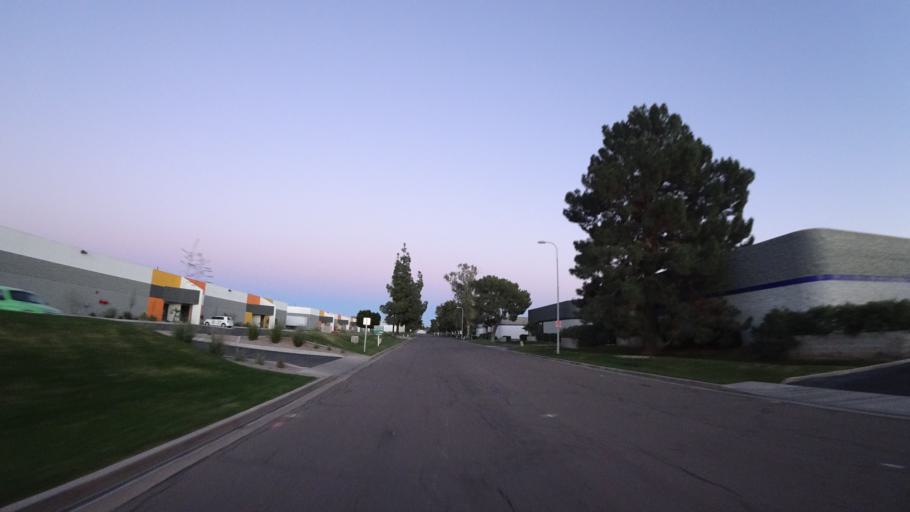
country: US
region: Arizona
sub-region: Maricopa County
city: Tempe Junction
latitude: 33.4156
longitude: -111.9663
